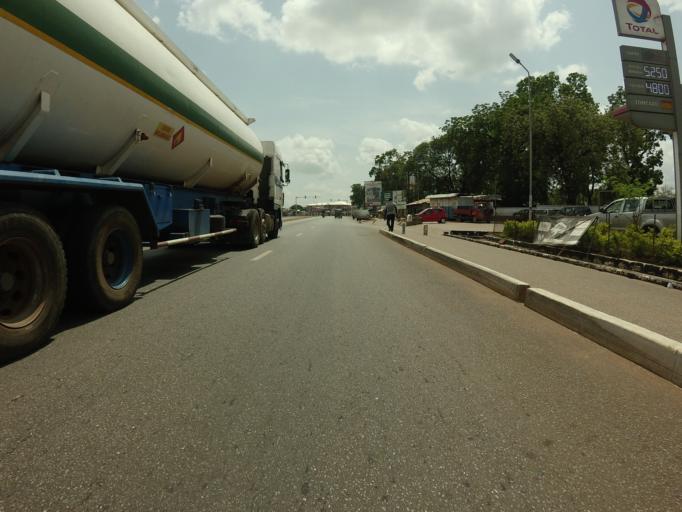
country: GH
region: Northern
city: Tamale
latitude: 9.4014
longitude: -0.8373
